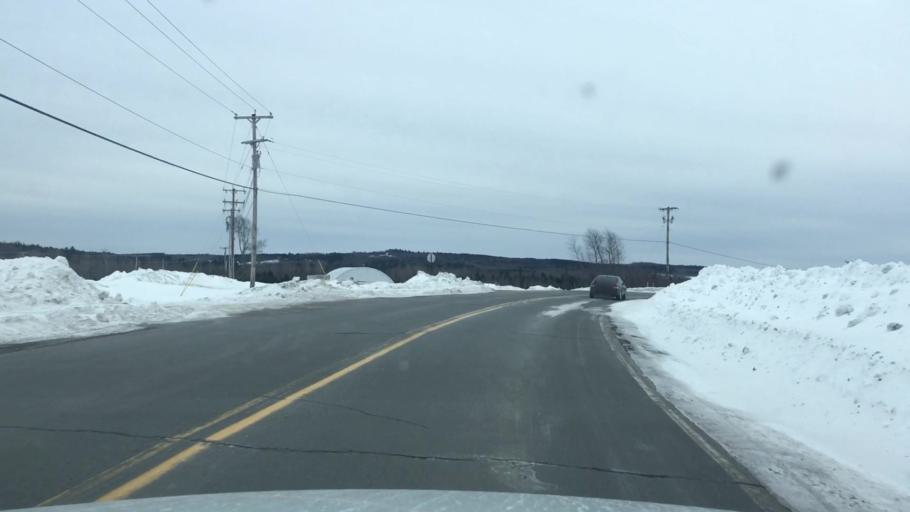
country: US
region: Maine
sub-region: Penobscot County
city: Garland
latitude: 44.9771
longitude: -69.0904
